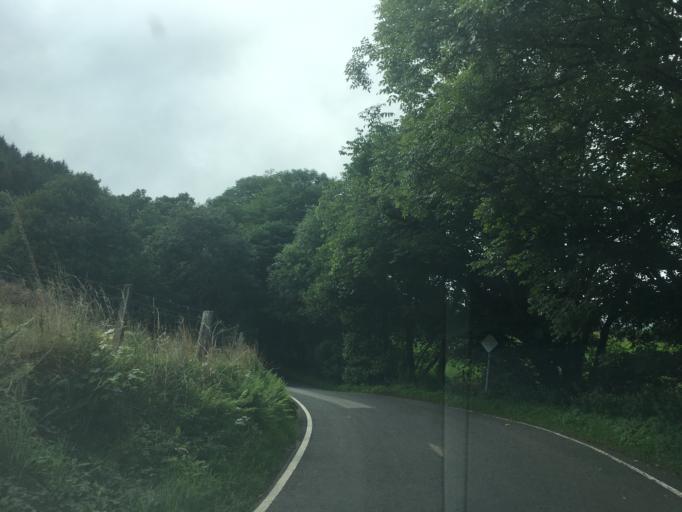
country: GB
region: Scotland
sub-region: Argyll and Bute
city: Ardrishaig
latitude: 56.0840
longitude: -5.5552
